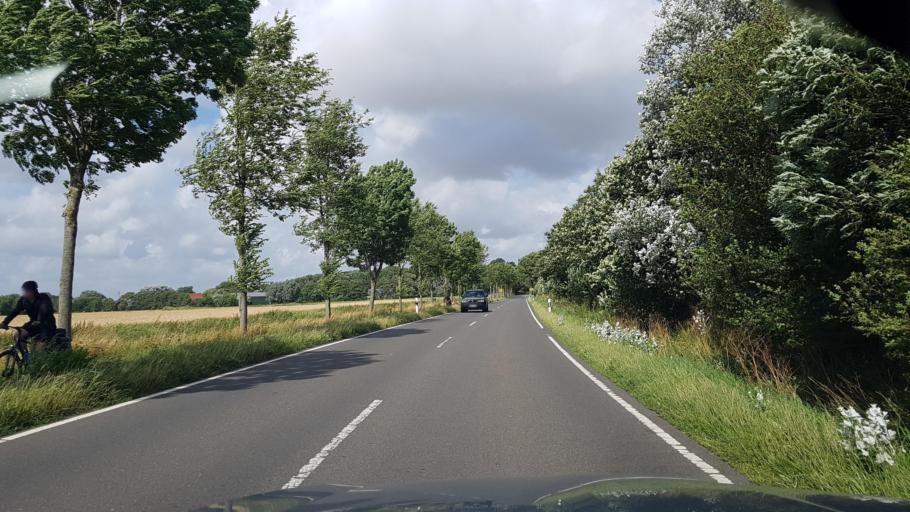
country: DE
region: Schleswig-Holstein
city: Suderdeich
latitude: 54.1967
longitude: 8.9038
